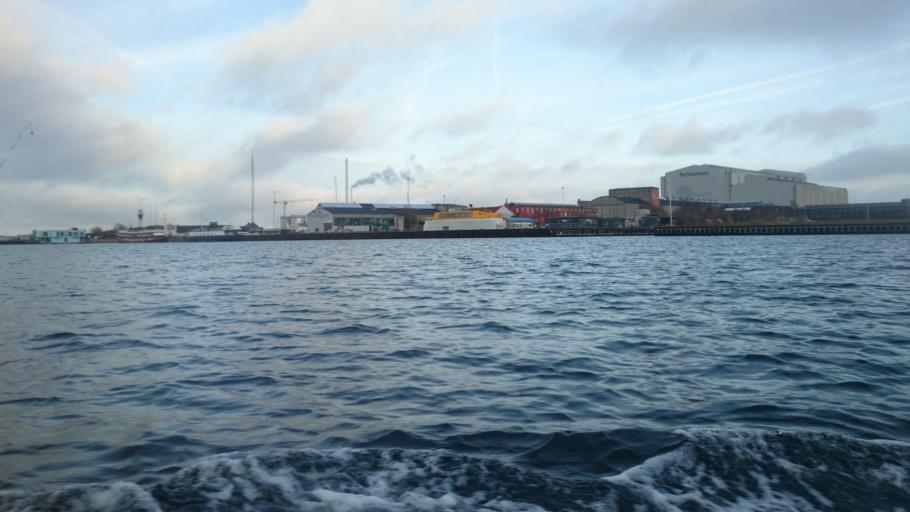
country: DK
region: Capital Region
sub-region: Kobenhavn
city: Christianshavn
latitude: 55.6920
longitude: 12.6046
